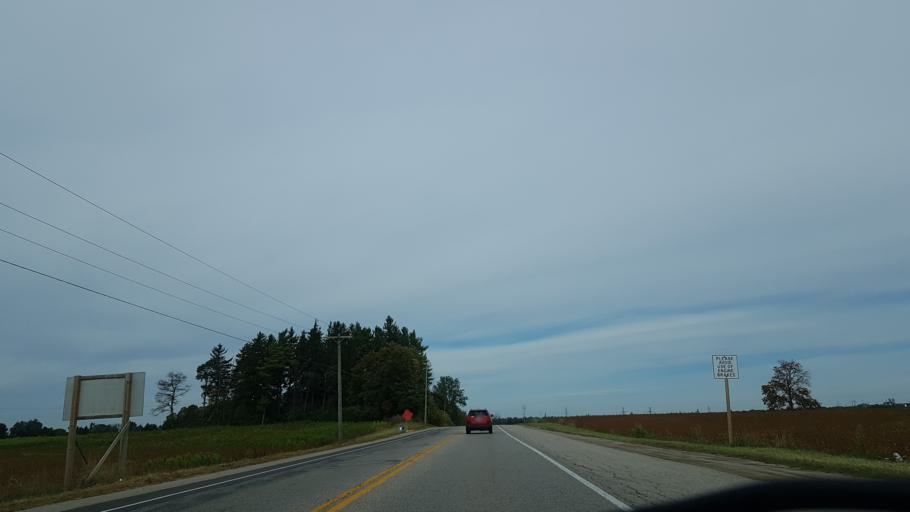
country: CA
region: Ontario
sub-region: Wellington County
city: Guelph
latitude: 43.5094
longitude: -80.2662
